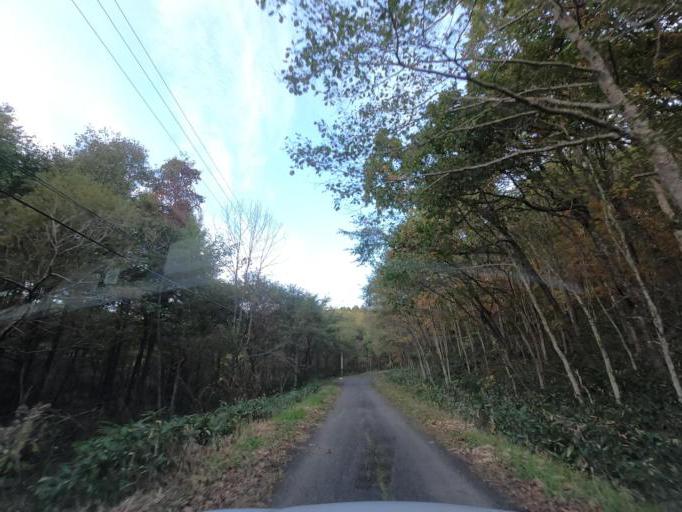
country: JP
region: Hokkaido
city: Obihiro
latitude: 42.5865
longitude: 143.3080
